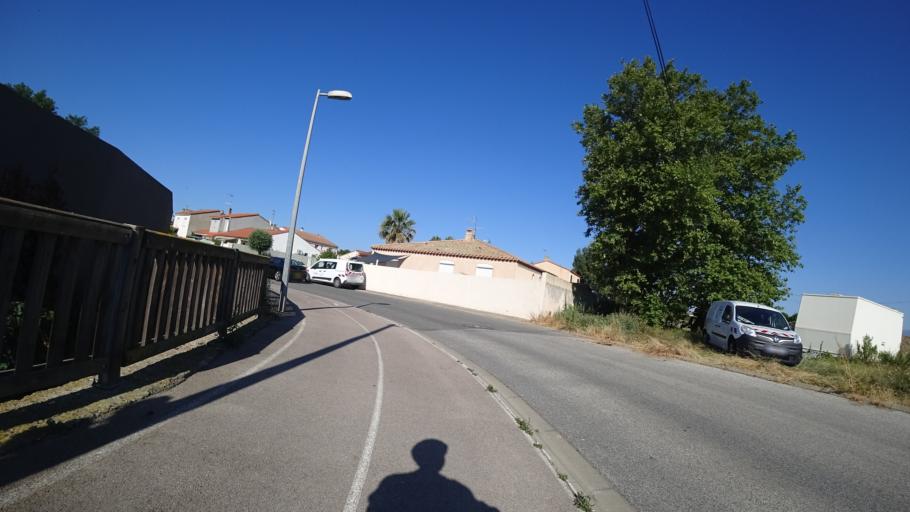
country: FR
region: Languedoc-Roussillon
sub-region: Departement des Pyrenees-Orientales
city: Sainte-Marie-Plage
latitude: 42.7293
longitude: 3.0158
